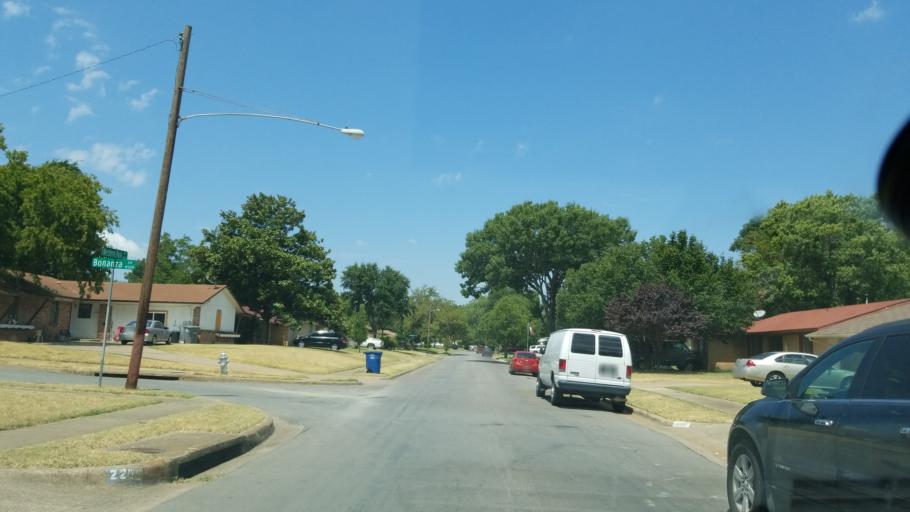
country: US
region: Texas
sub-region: Dallas County
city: Cockrell Hill
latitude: 32.7234
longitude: -96.8951
